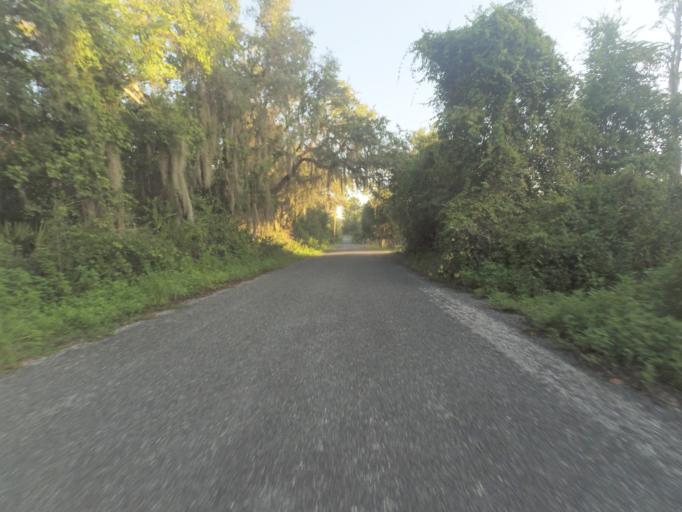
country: US
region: Florida
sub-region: Lake County
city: Astor
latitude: 29.2791
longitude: -81.6455
